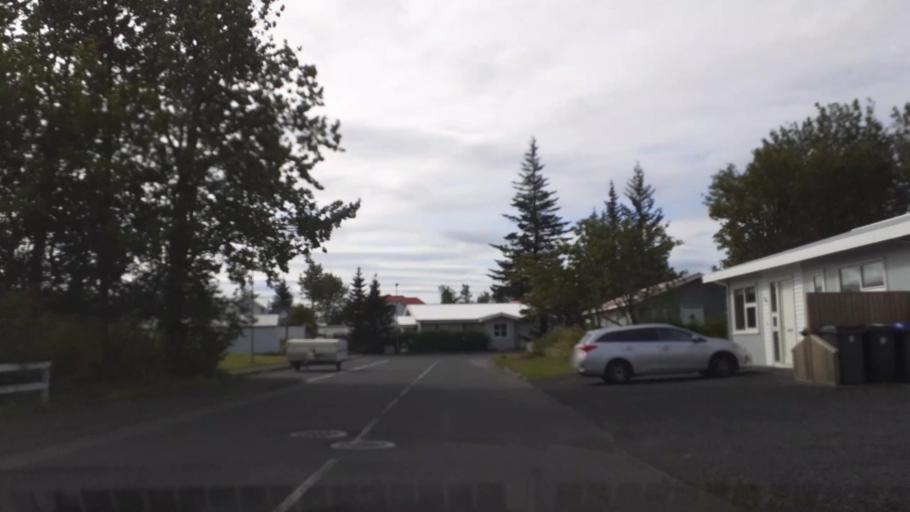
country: IS
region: South
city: Vestmannaeyjar
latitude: 63.8389
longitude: -20.3990
